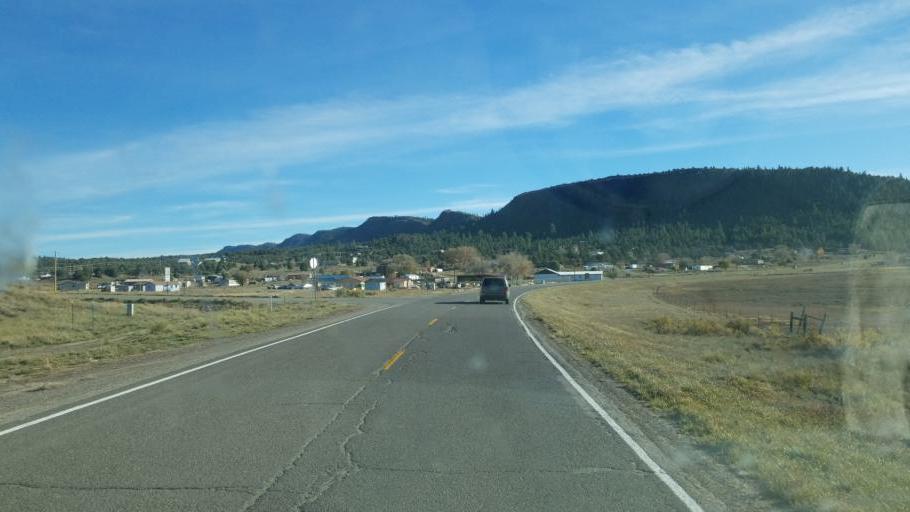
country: US
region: New Mexico
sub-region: Rio Arriba County
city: Dulce
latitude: 36.9212
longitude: -106.9922
